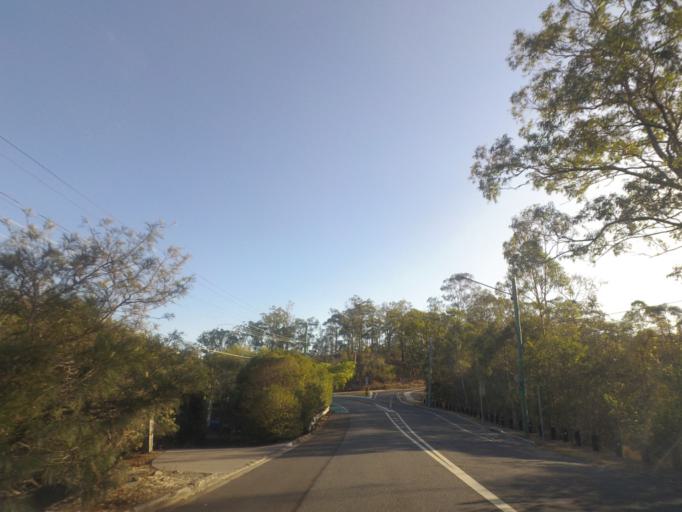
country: AU
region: Queensland
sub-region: Brisbane
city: Taringa
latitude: -27.4723
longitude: 152.9718
